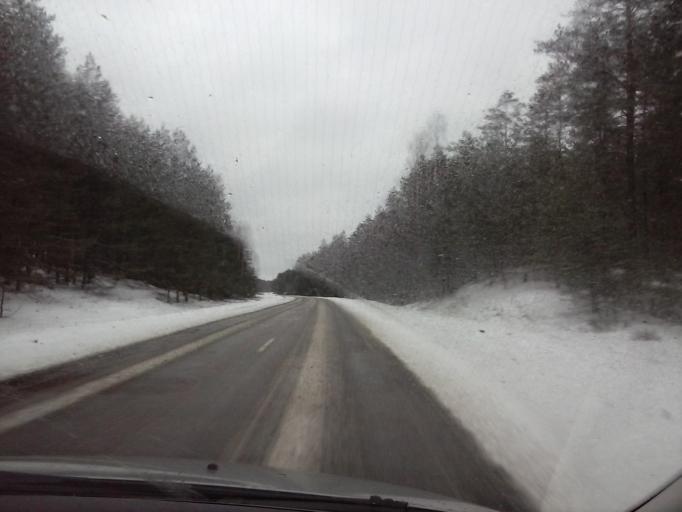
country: LV
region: Strenci
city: Seda
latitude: 57.6583
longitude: 25.8714
